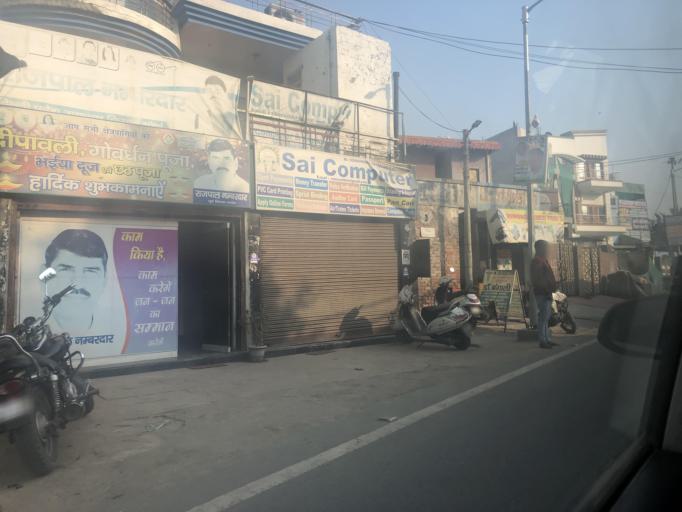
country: IN
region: Haryana
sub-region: Gurgaon
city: Gurgaon
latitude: 28.5621
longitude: 77.0016
